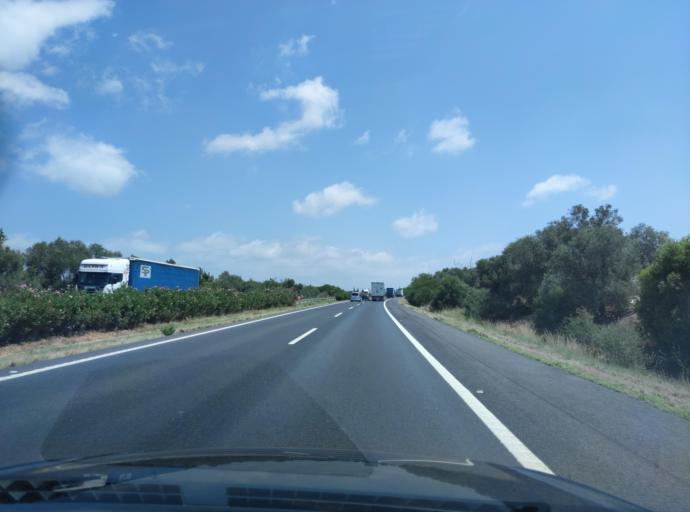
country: ES
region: Catalonia
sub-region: Provincia de Tarragona
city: Masdenverge
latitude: 40.6918
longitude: 0.5316
